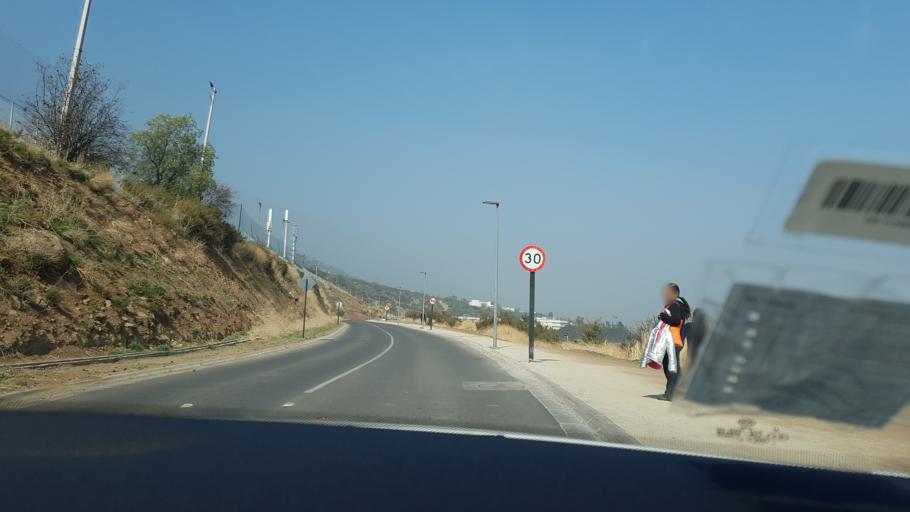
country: CL
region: Santiago Metropolitan
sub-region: Provincia de Santiago
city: Villa Presidente Frei, Nunoa, Santiago, Chile
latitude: -33.4777
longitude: -70.5171
